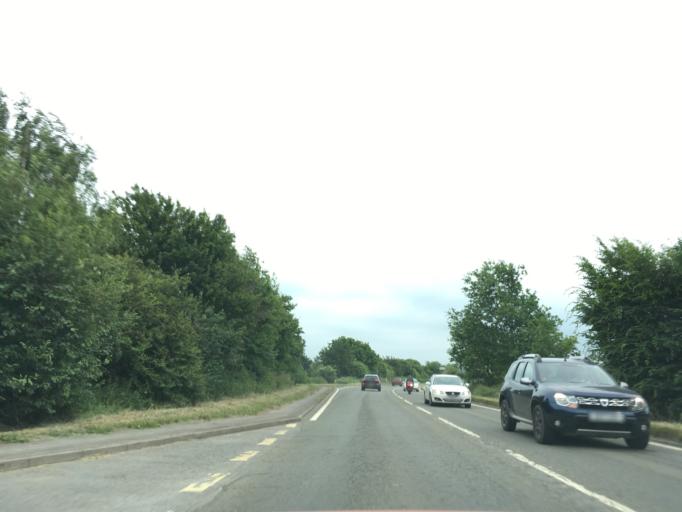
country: GB
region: England
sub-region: Gloucestershire
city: Dursley
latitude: 51.7231
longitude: -2.3713
